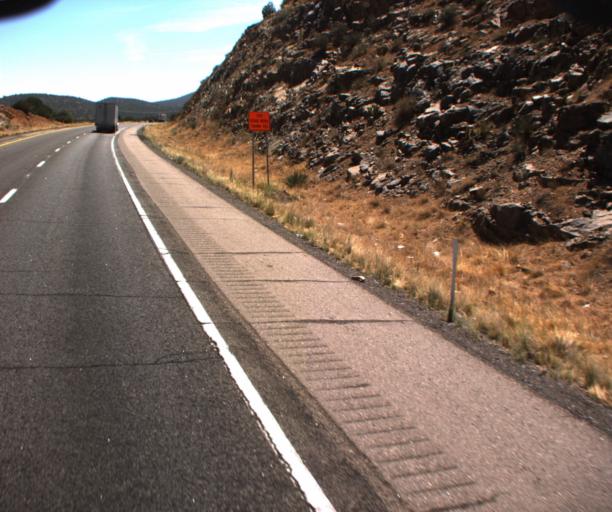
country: US
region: Arizona
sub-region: Mohave County
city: Peach Springs
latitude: 35.1810
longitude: -113.4661
